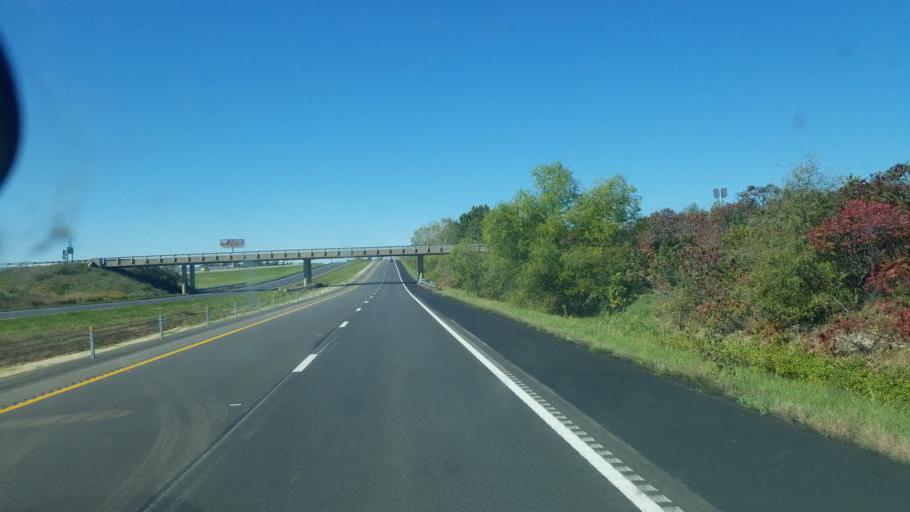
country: US
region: Missouri
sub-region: Lafayette County
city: Odessa
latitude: 39.0078
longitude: -93.9407
